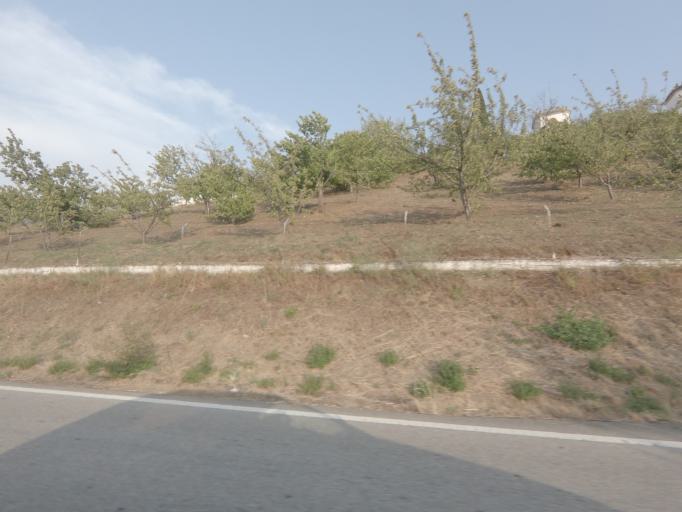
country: PT
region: Viseu
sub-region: Armamar
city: Armamar
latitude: 41.1498
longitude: -7.6846
